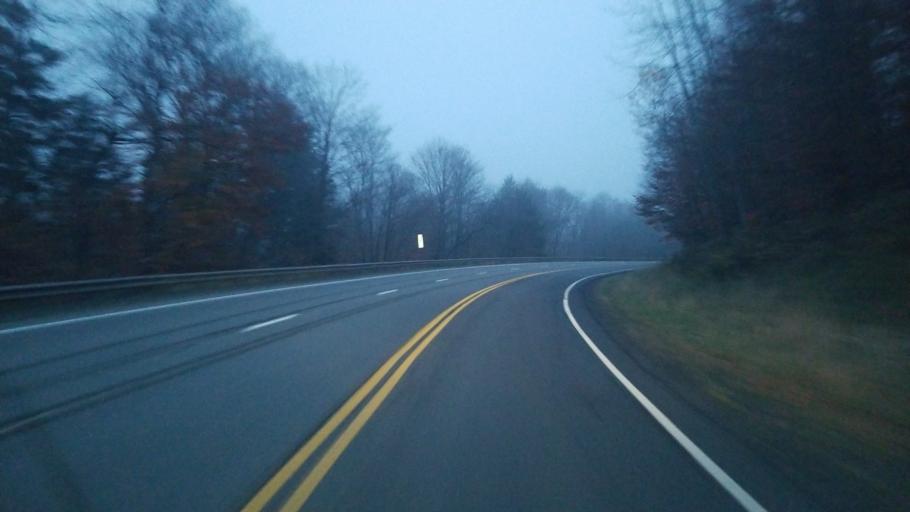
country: US
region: Pennsylvania
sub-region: McKean County
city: Smethport
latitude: 41.7231
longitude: -78.6160
